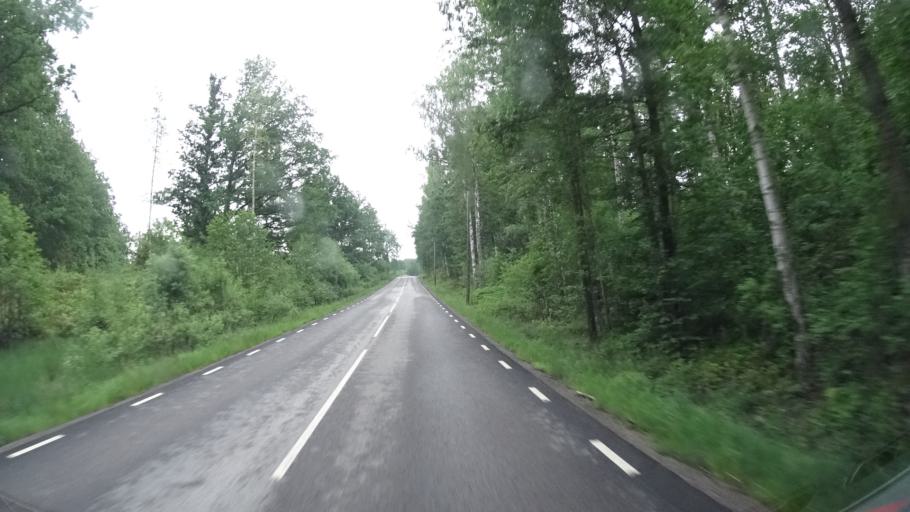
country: SE
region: Kalmar
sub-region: Oskarshamns Kommun
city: Oskarshamn
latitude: 57.3664
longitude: 16.2284
